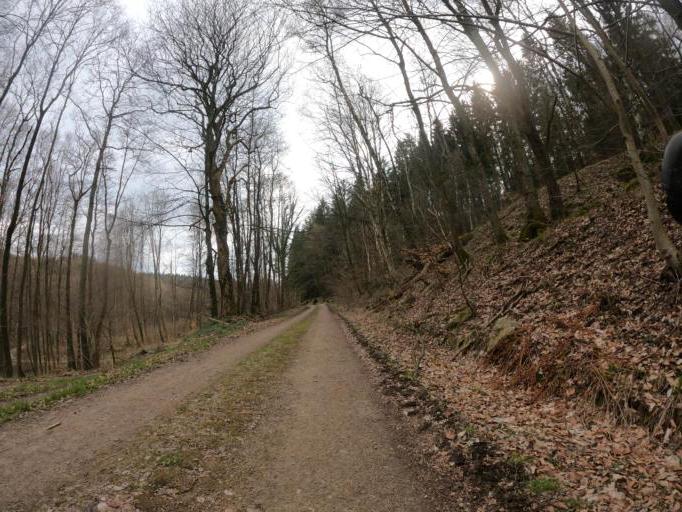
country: DE
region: North Rhine-Westphalia
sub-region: Regierungsbezirk Koln
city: Hurtgenwald
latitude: 50.6918
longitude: 6.3376
